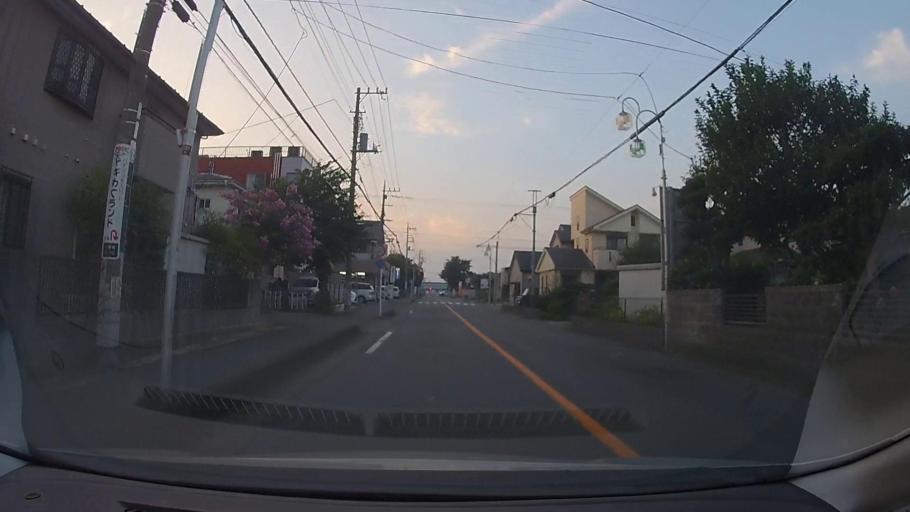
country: JP
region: Kanagawa
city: Minami-rinkan
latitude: 35.4763
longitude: 139.4545
